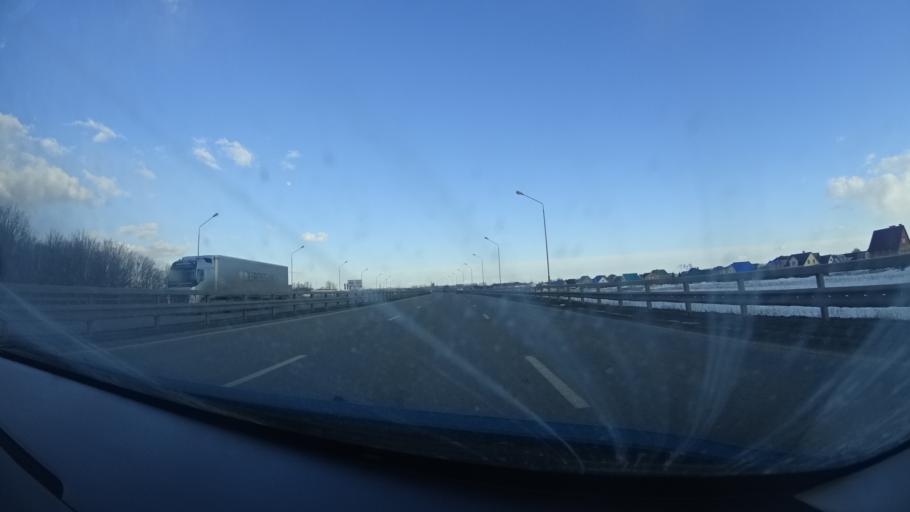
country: RU
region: Bashkortostan
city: Ufa
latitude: 54.6477
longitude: 55.9146
